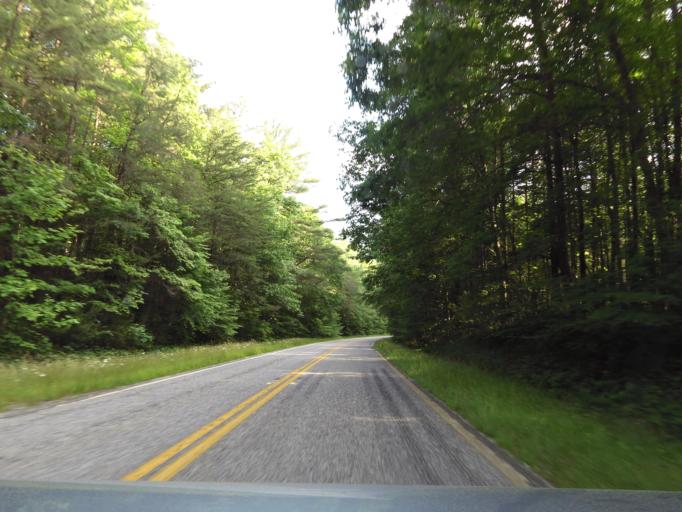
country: US
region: Georgia
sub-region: Towns County
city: Hiawassee
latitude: 34.8360
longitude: -83.8041
